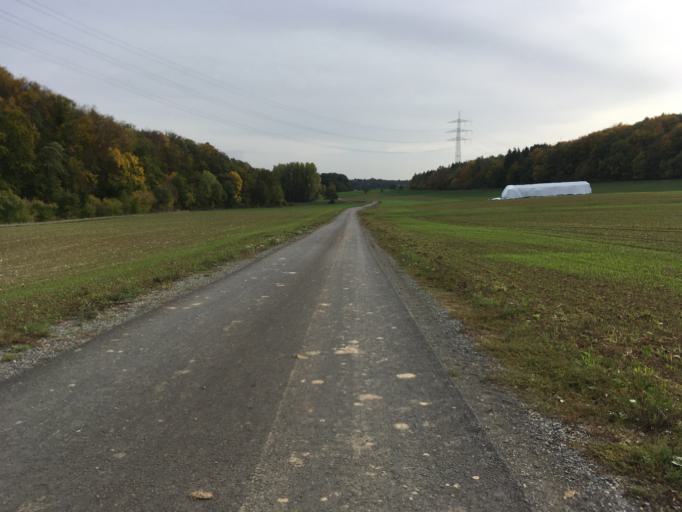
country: DE
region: Baden-Wuerttemberg
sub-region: Karlsruhe Region
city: Buchen
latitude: 49.4864
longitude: 9.3420
